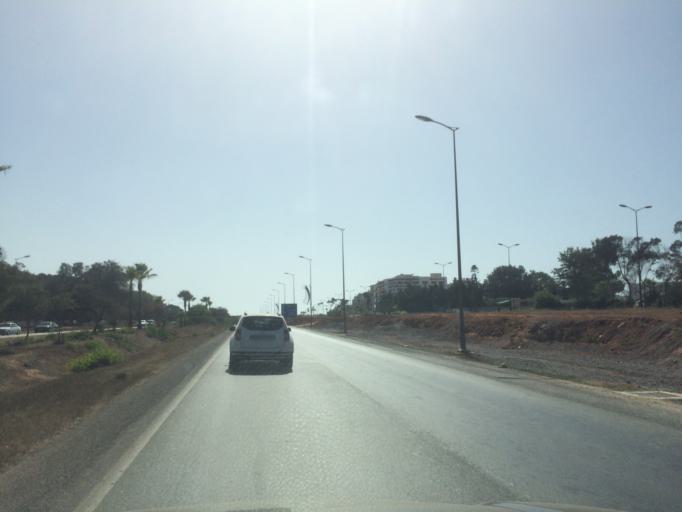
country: MA
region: Rabat-Sale-Zemmour-Zaer
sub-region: Skhirate-Temara
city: Temara
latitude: 33.9661
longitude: -6.8914
